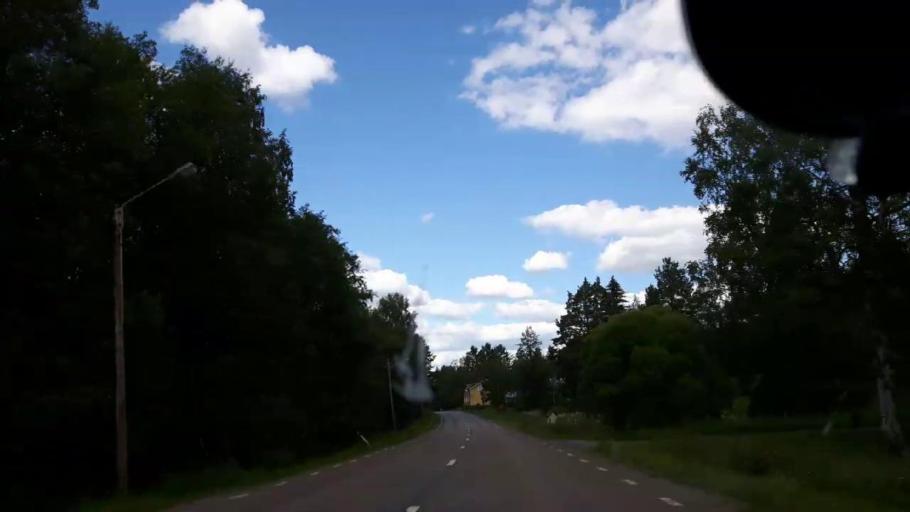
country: SE
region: Jaemtland
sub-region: Ragunda Kommun
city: Hammarstrand
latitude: 62.9975
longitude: 16.6769
